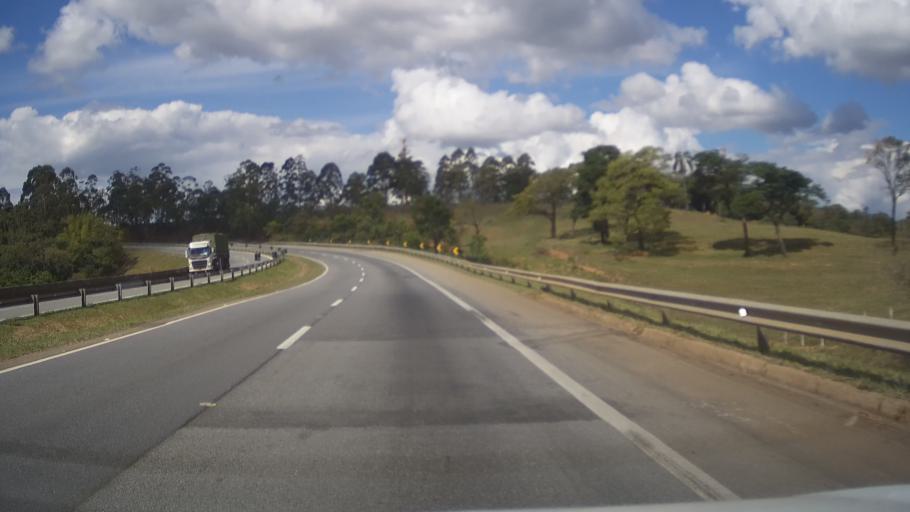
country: BR
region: Minas Gerais
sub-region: Oliveira
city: Oliveira
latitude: -20.8260
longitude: -44.8029
